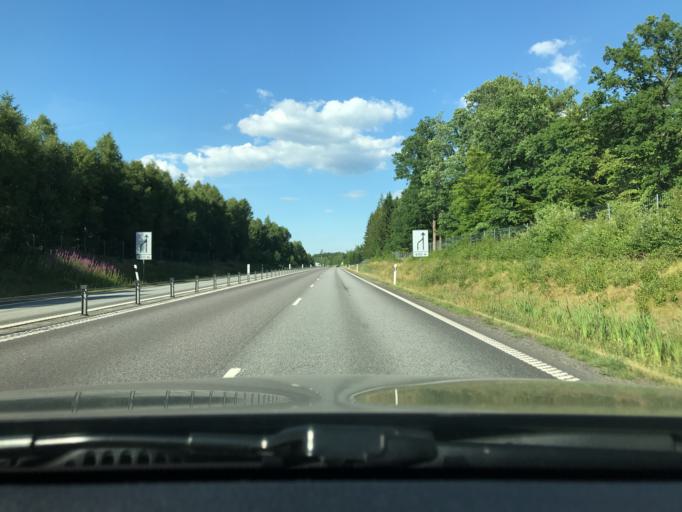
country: SE
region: Kronoberg
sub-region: Almhults Kommun
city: AElmhult
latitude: 56.4537
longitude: 14.0871
